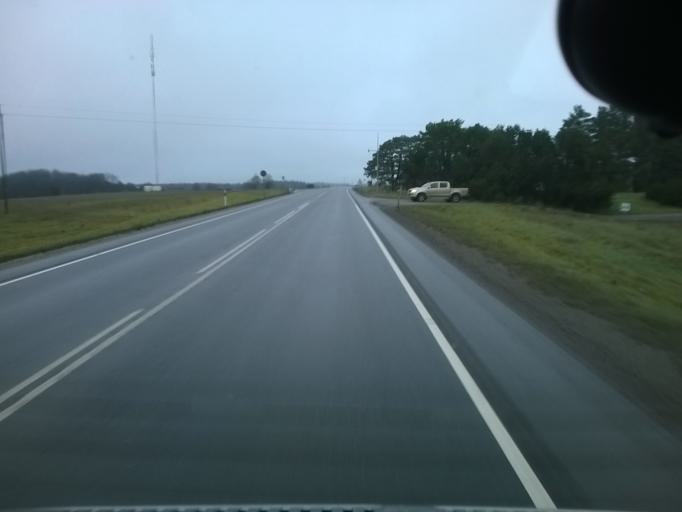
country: EE
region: Harju
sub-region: Saku vald
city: Saku
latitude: 59.2795
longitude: 24.7412
